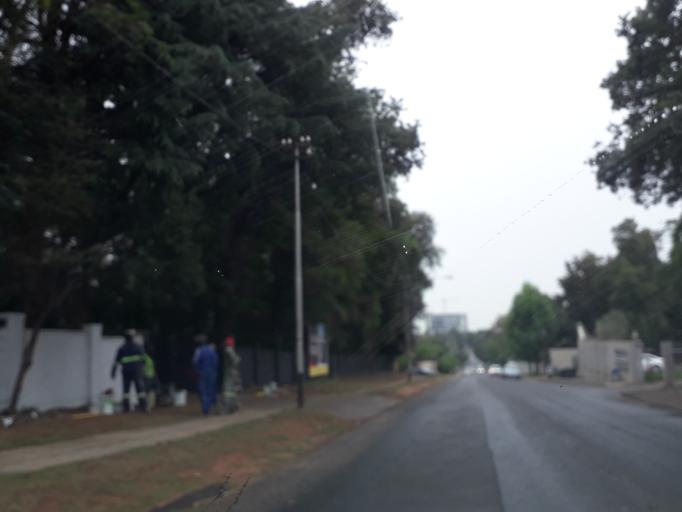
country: ZA
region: Gauteng
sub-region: City of Johannesburg Metropolitan Municipality
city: Johannesburg
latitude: -26.1339
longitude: 28.0449
